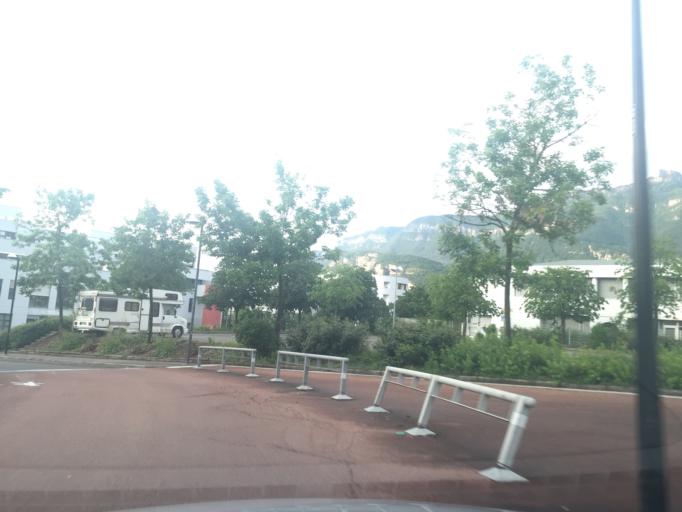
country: FR
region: Rhone-Alpes
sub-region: Departement de la Savoie
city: Bassens
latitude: 45.5914
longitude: 5.9194
